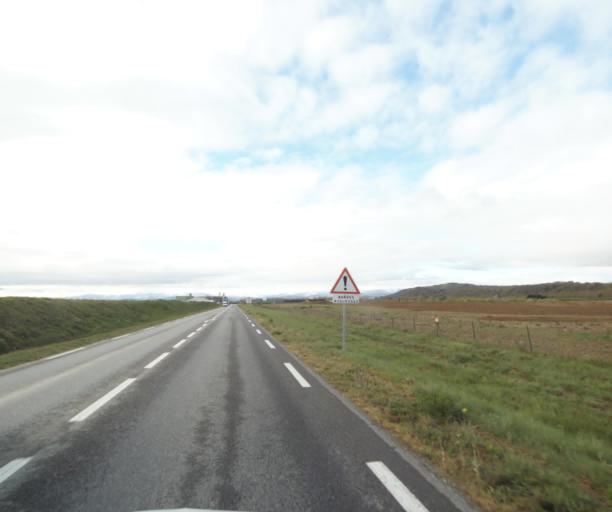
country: FR
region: Midi-Pyrenees
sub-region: Departement de l'Ariege
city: Saverdun
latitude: 43.2077
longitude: 1.6085
